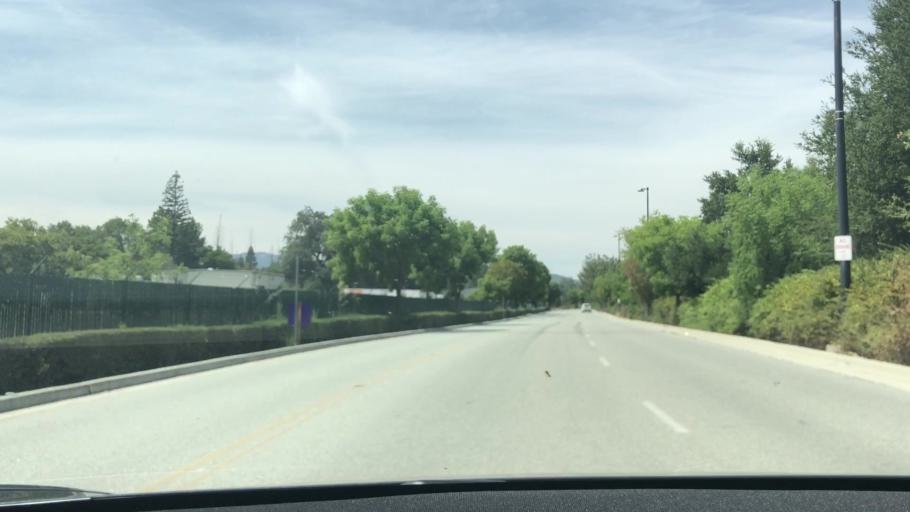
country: US
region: California
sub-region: Santa Clara County
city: Gilroy
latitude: 37.0079
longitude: -121.6245
